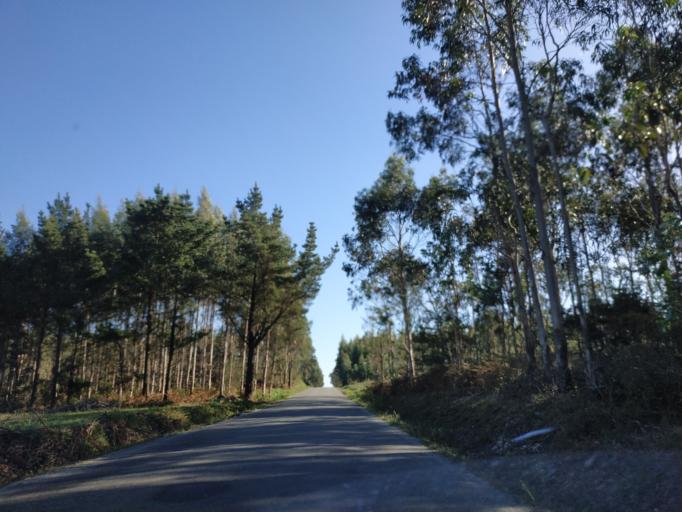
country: ES
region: Galicia
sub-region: Provincia da Coruna
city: Santa Comba
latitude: 43.0217
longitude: -8.7418
